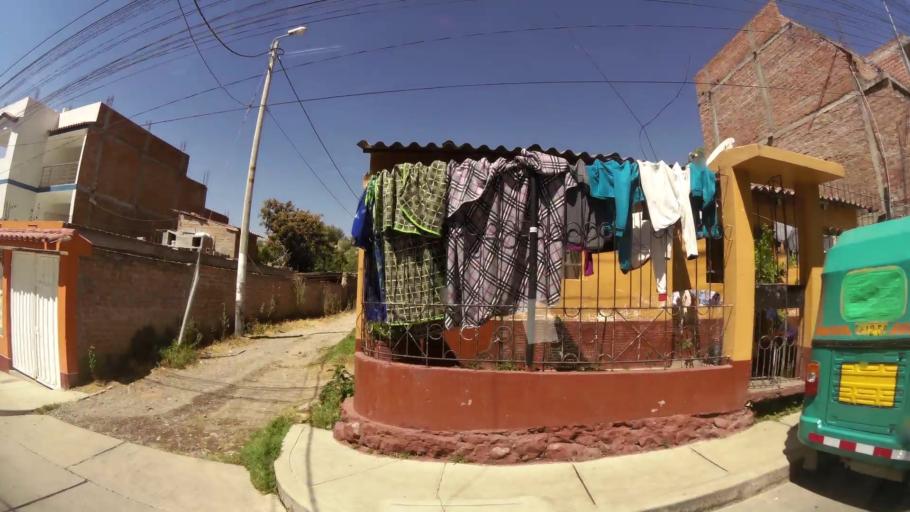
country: PE
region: Ayacucho
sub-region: Provincia de Huamanga
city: Ayacucho
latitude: -13.1683
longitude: -74.2338
